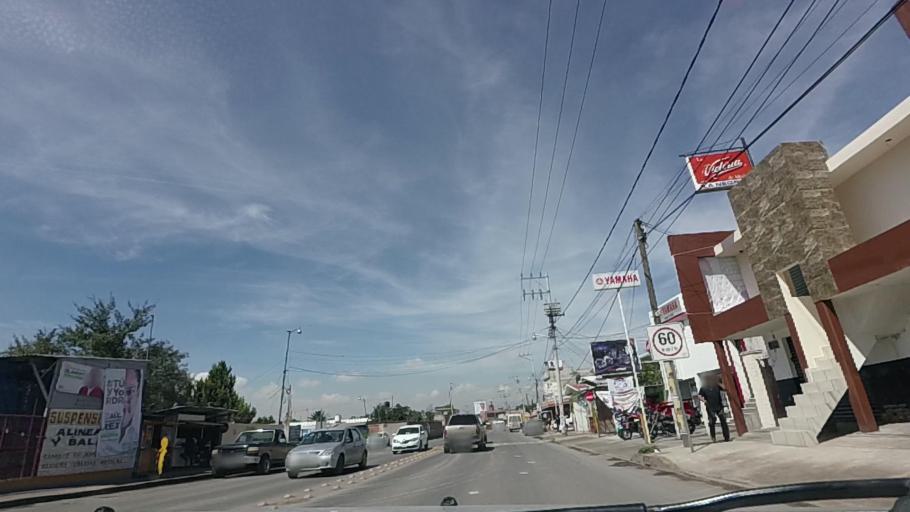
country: MX
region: Mexico
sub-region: Cuautitlan
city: Barrio Tlatenco
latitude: 19.7368
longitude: -99.1825
